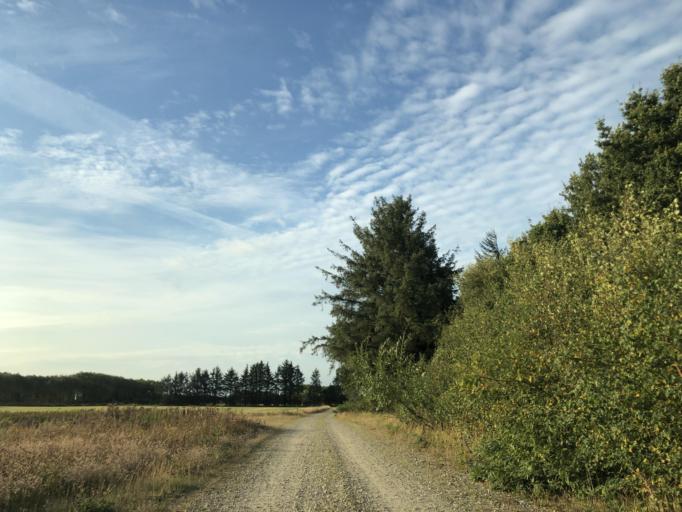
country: DK
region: Central Jutland
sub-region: Holstebro Kommune
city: Ulfborg
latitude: 56.2584
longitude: 8.3208
